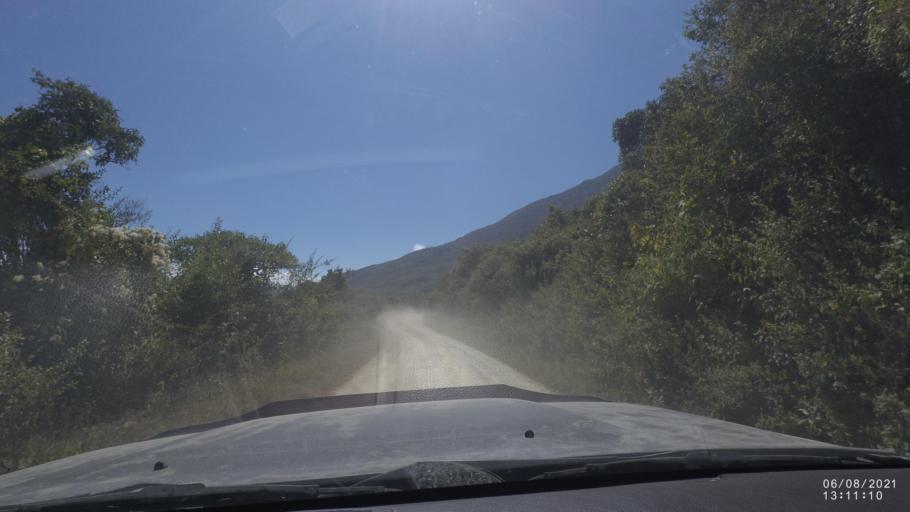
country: BO
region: La Paz
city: Quime
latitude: -16.7213
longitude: -66.7060
